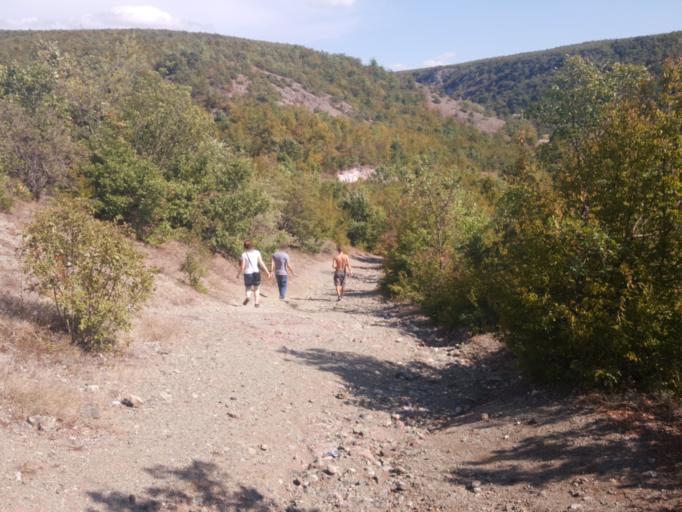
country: XK
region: Pec
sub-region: Komuna e Klines
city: Klina
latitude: 42.5264
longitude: 20.5715
